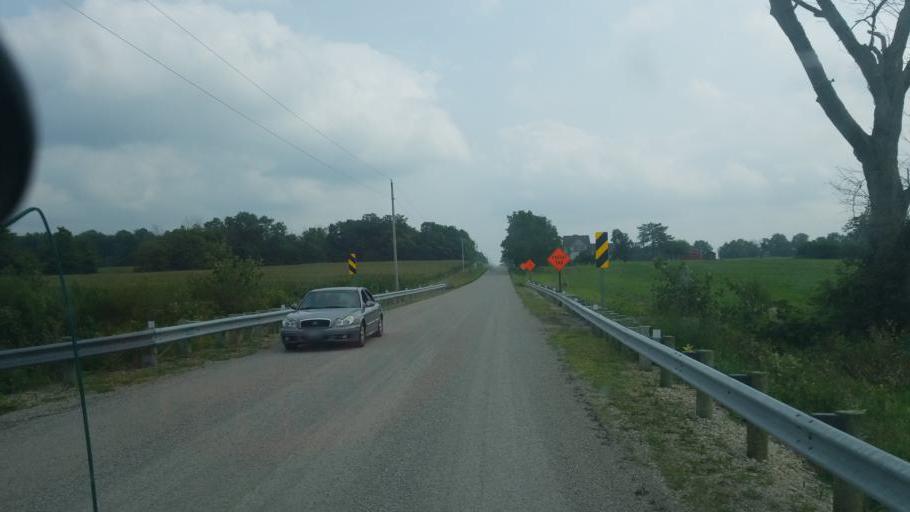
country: US
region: Ohio
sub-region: Huron County
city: Greenwich
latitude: 41.0661
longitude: -82.5338
